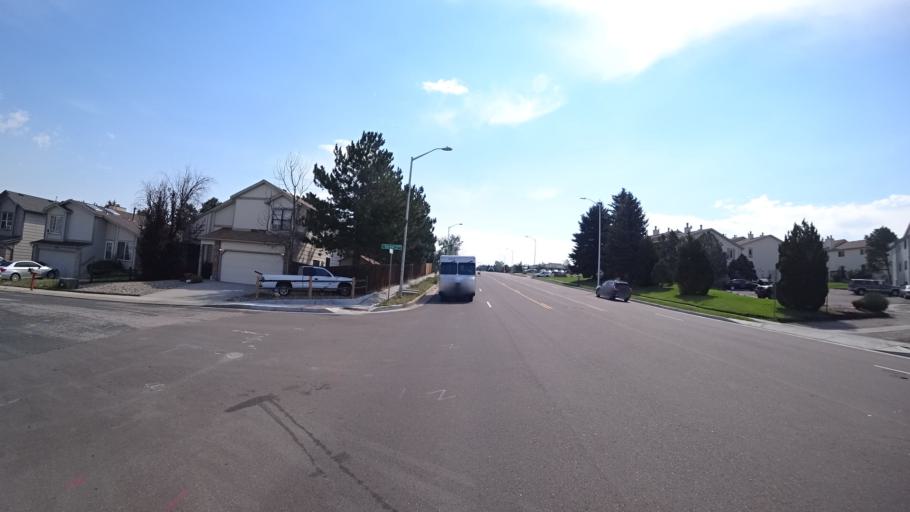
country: US
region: Colorado
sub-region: El Paso County
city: Colorado Springs
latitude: 38.9259
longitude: -104.7810
